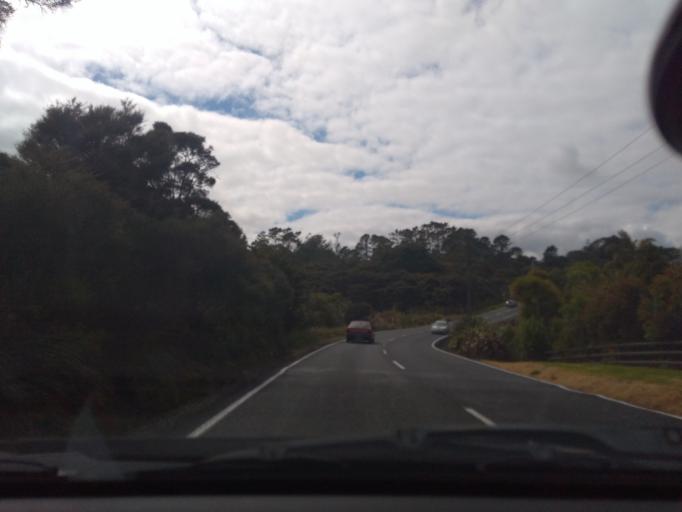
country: NZ
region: Auckland
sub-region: Auckland
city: Muriwai Beach
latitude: -36.8586
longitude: 174.5518
